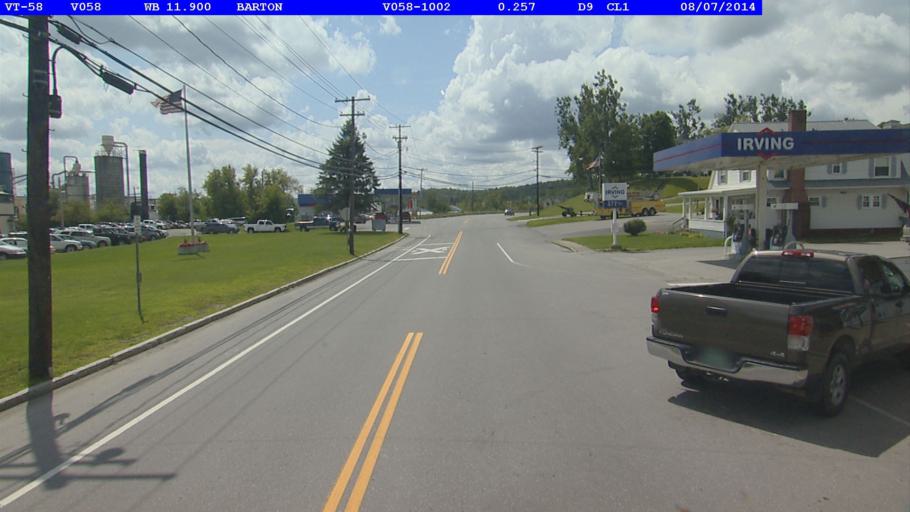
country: US
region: Vermont
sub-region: Orleans County
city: Newport
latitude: 44.8099
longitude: -72.2041
